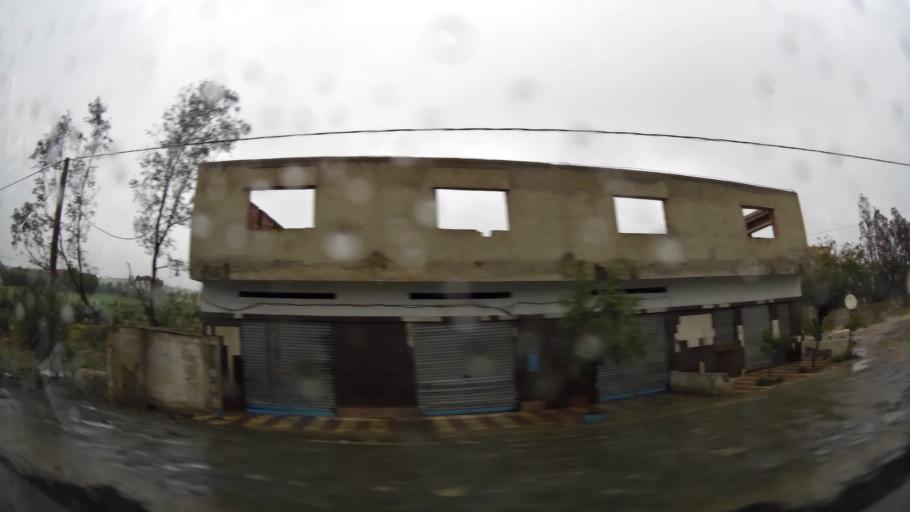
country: MA
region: Taza-Al Hoceima-Taounate
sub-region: Taza
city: Aknoul
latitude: 34.8007
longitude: -3.7411
